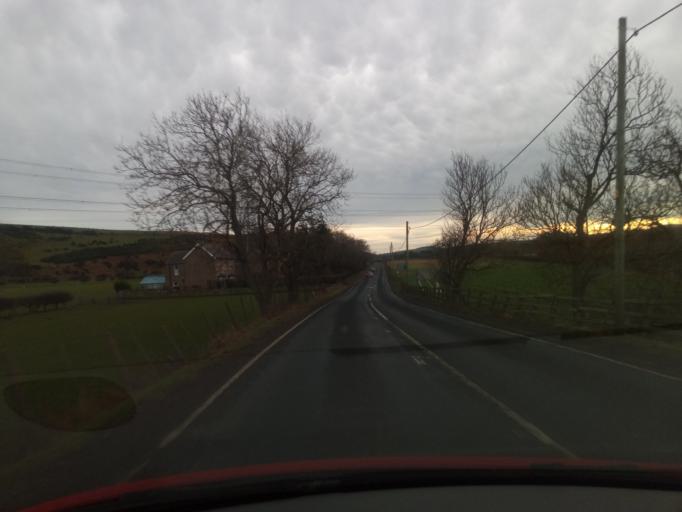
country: GB
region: England
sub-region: Northumberland
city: Wooler
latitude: 55.5391
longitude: -2.0046
